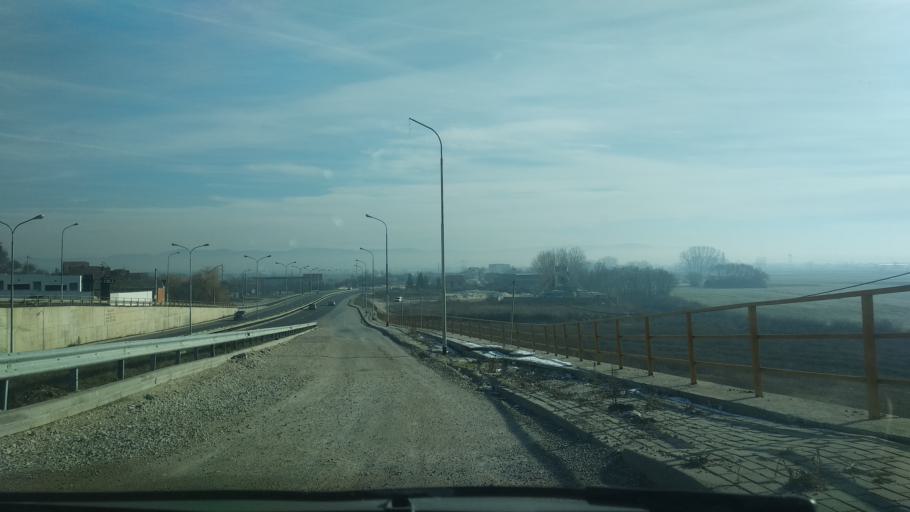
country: XK
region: Pristina
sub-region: Komuna e Obiliqit
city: Obiliq
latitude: 42.7381
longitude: 21.0557
